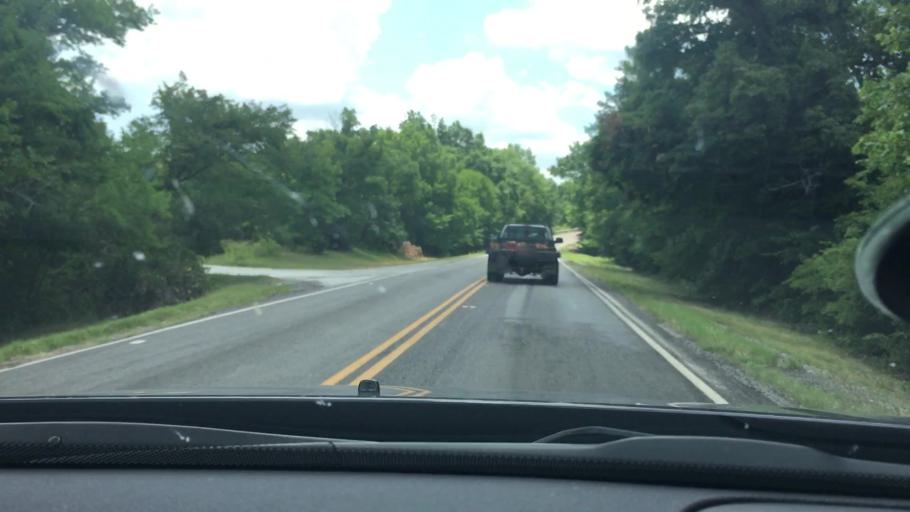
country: US
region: Oklahoma
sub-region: Pontotoc County
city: Ada
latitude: 34.5746
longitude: -96.6299
